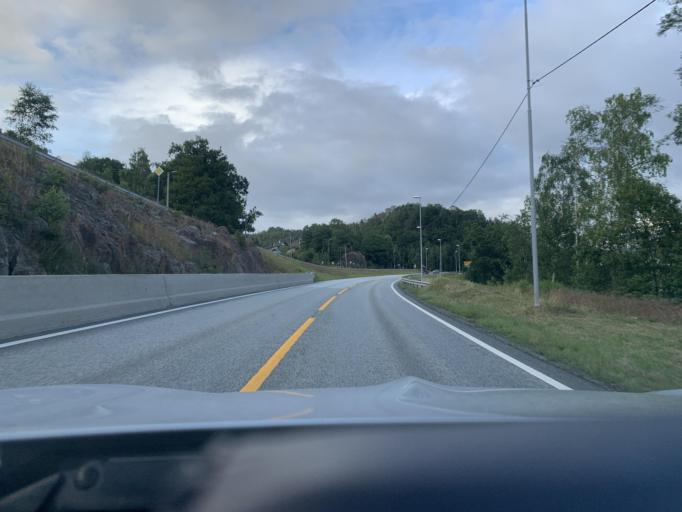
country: NO
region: Rogaland
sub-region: Bjerkreim
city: Vikesa
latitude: 58.5829
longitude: 6.0652
